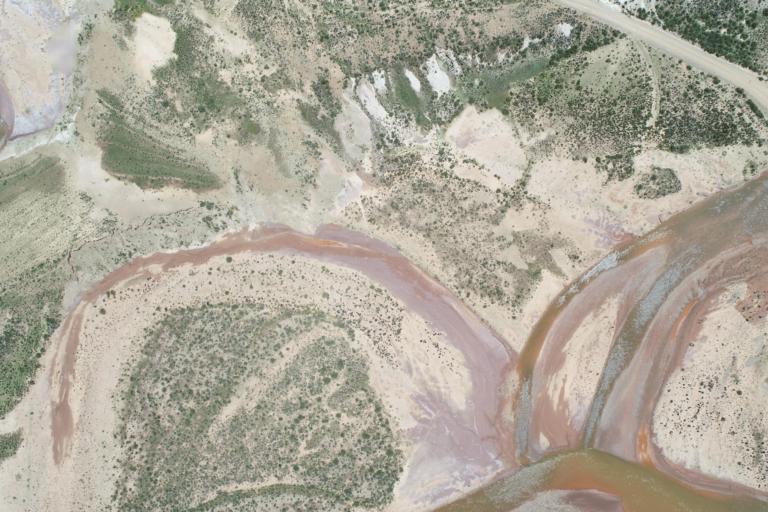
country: BO
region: La Paz
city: Curahuara de Carangas
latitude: -17.3090
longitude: -68.4966
